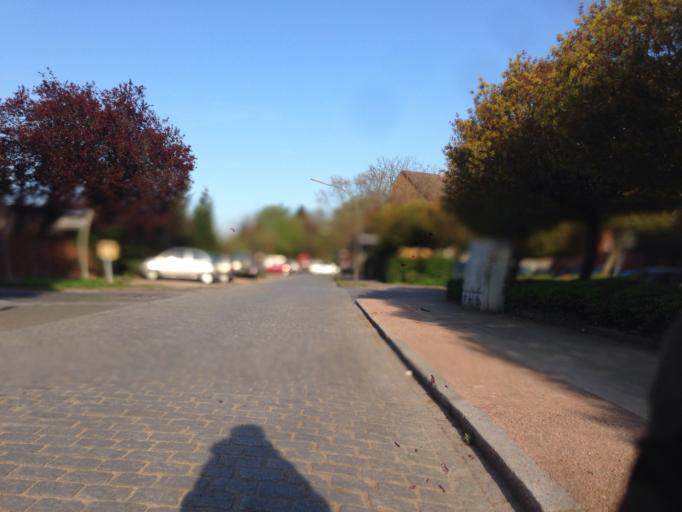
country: DE
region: Hamburg
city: Steilshoop
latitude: 53.5896
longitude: 10.0691
